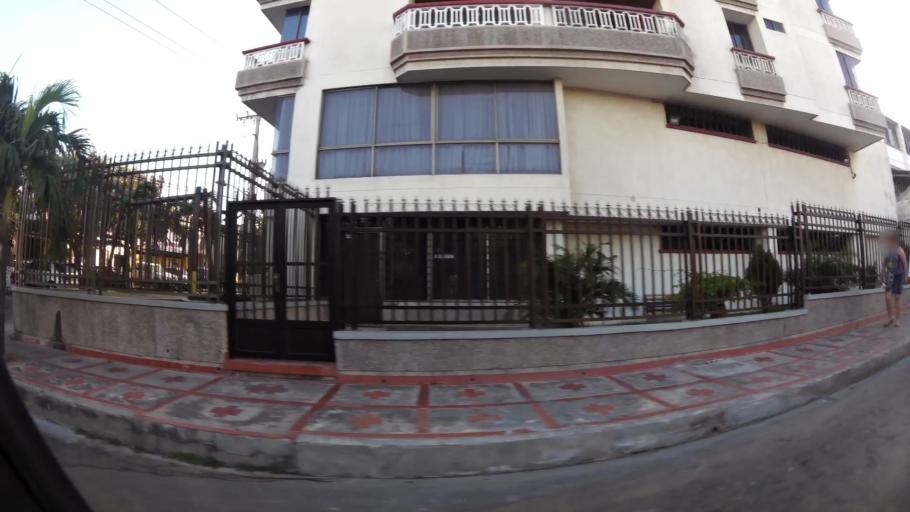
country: CO
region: Atlantico
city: Barranquilla
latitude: 10.9839
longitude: -74.7997
